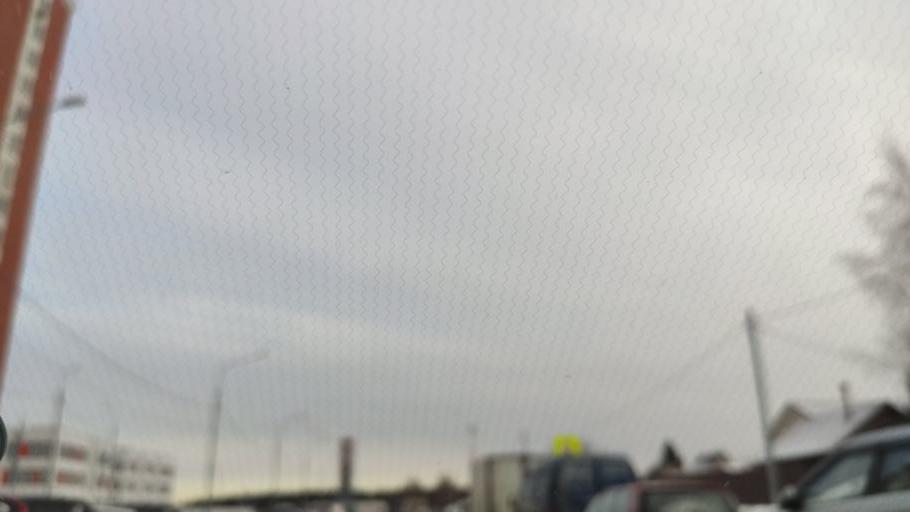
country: RU
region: Moscow
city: Annino
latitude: 55.5282
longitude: 37.6180
